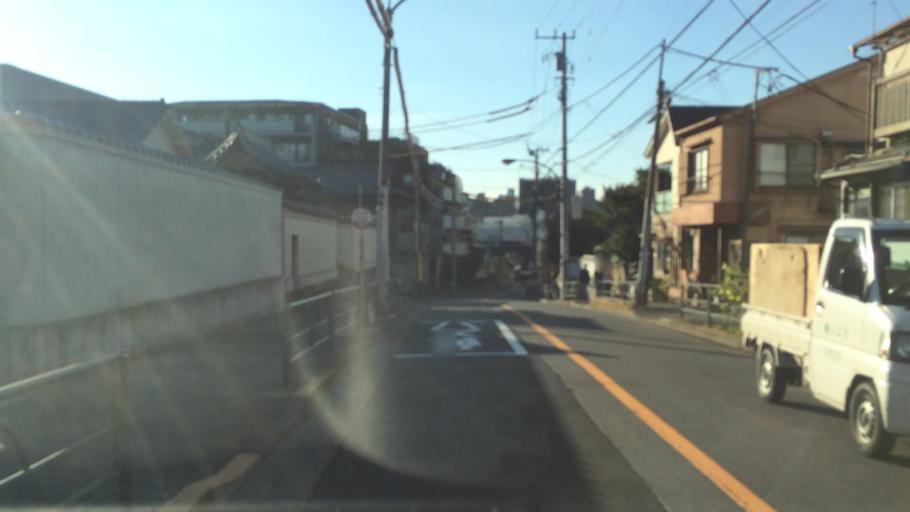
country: JP
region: Tokyo
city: Tokyo
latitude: 35.7237
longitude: 139.7675
